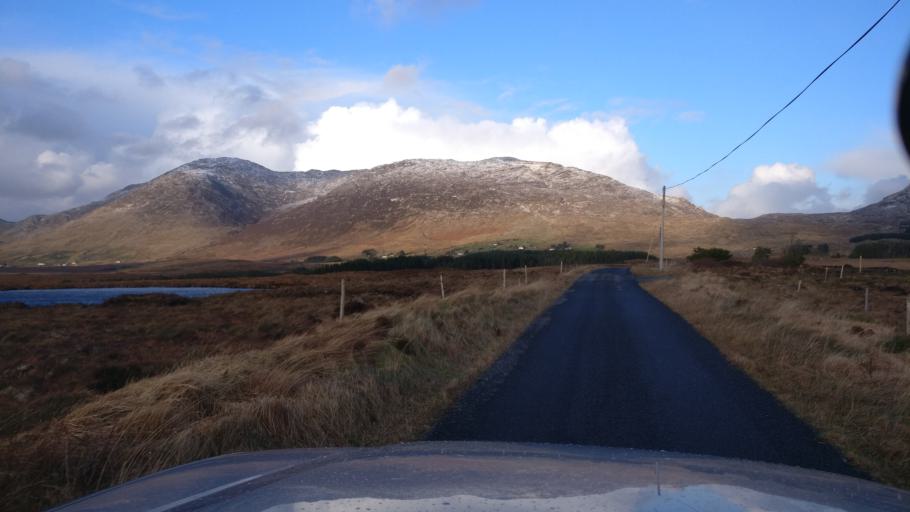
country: IE
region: Connaught
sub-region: County Galway
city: Clifden
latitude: 53.4737
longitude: -9.6894
